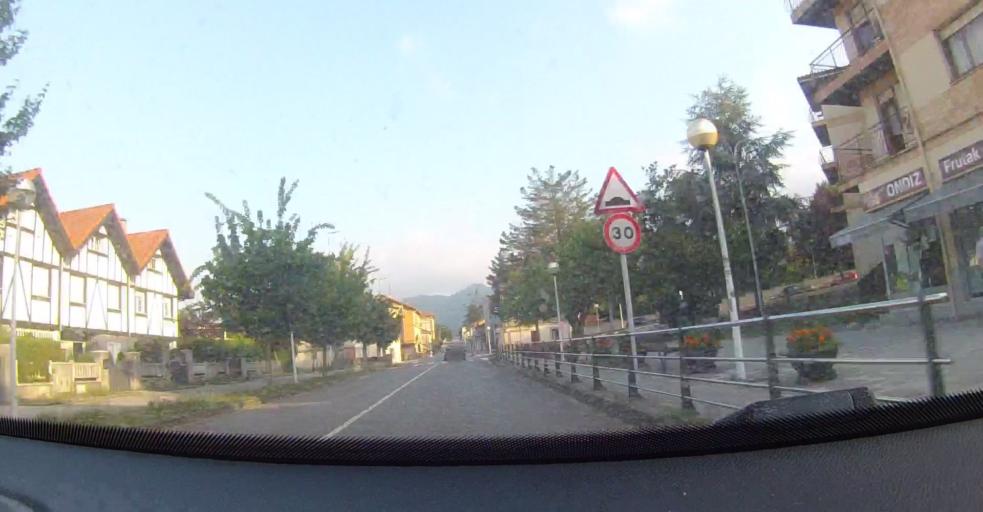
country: ES
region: Basque Country
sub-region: Bizkaia
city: Sopuerta
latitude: 43.2748
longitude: -3.1572
